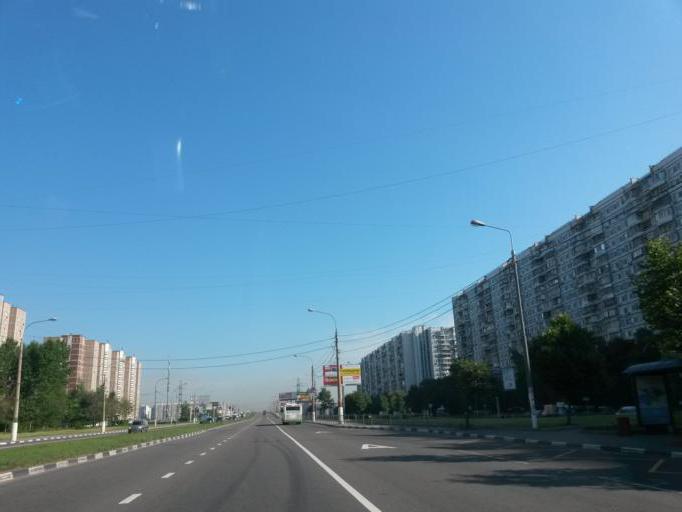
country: RU
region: Moscow
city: Brateyevo
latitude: 55.6329
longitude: 37.7507
